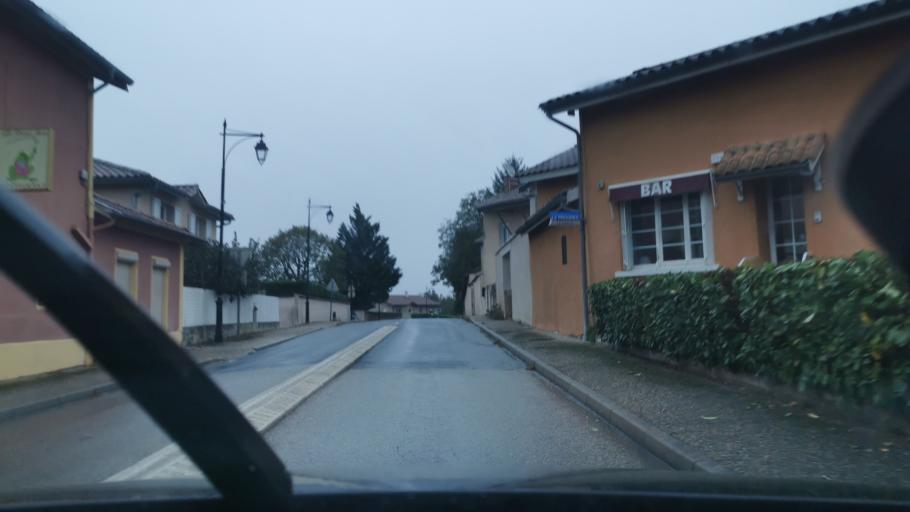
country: FR
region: Rhone-Alpes
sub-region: Departement de l'Ain
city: Civrieux
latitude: 45.9519
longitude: 4.8826
